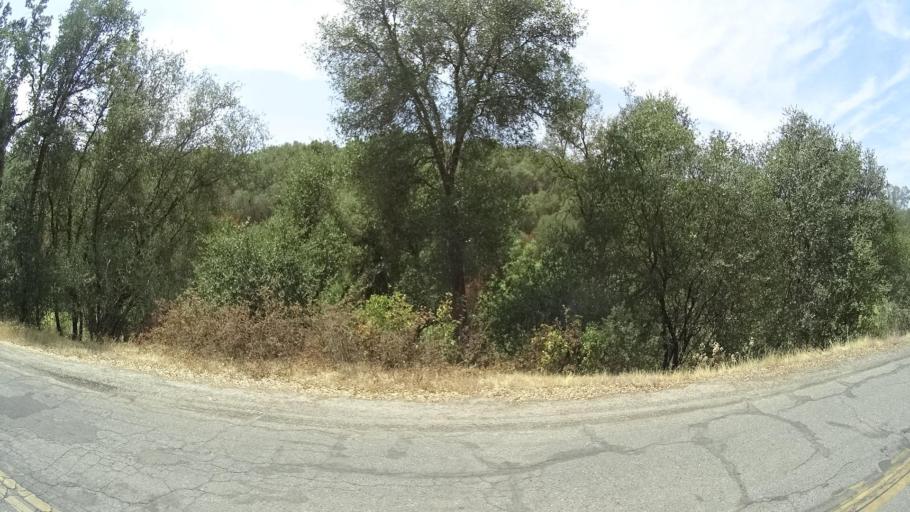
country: US
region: California
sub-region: Mariposa County
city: Mariposa
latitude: 37.4193
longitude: -119.8728
